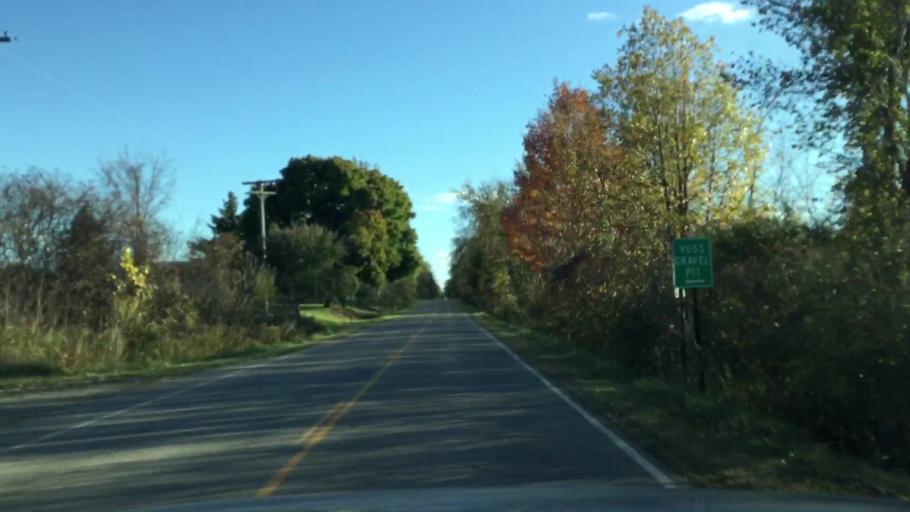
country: US
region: Michigan
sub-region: Lapeer County
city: Imlay City
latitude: 42.9982
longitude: -83.1839
